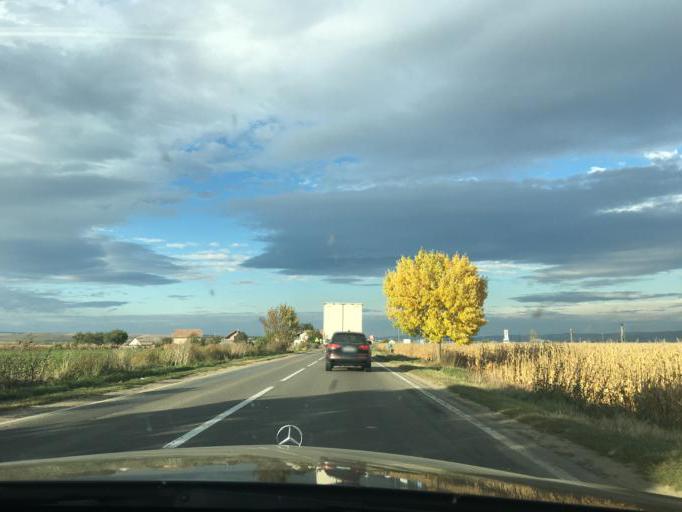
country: RO
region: Alba
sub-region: Comuna Galda de Jos
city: Galda de Jos
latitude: 46.1743
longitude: 23.6532
